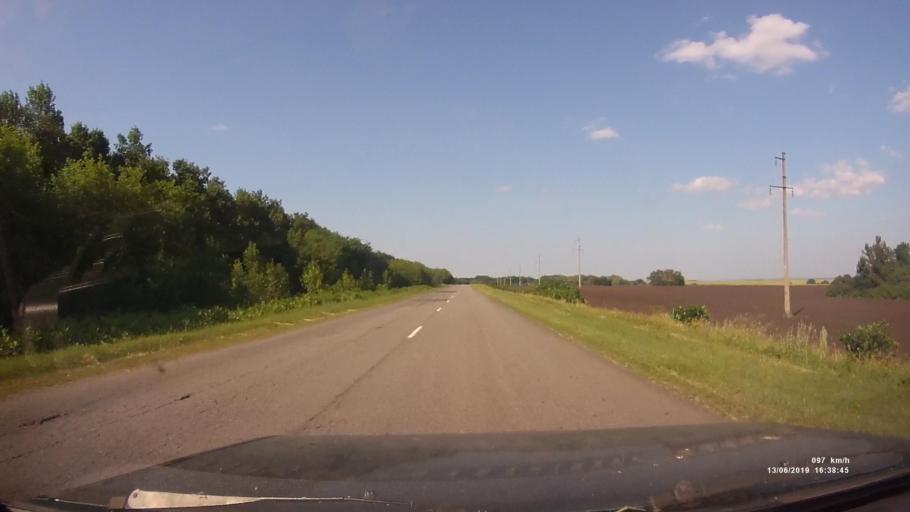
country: RU
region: Rostov
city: Kazanskaya
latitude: 49.9221
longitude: 41.3287
